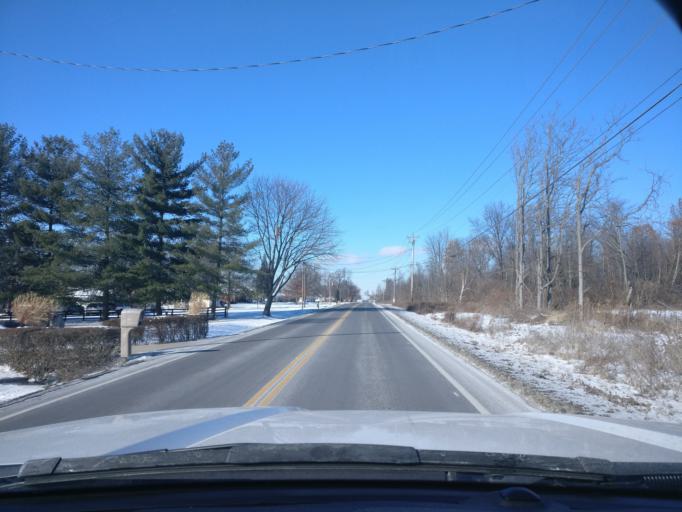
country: US
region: Ohio
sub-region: Warren County
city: Hunter
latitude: 39.4955
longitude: -84.2555
